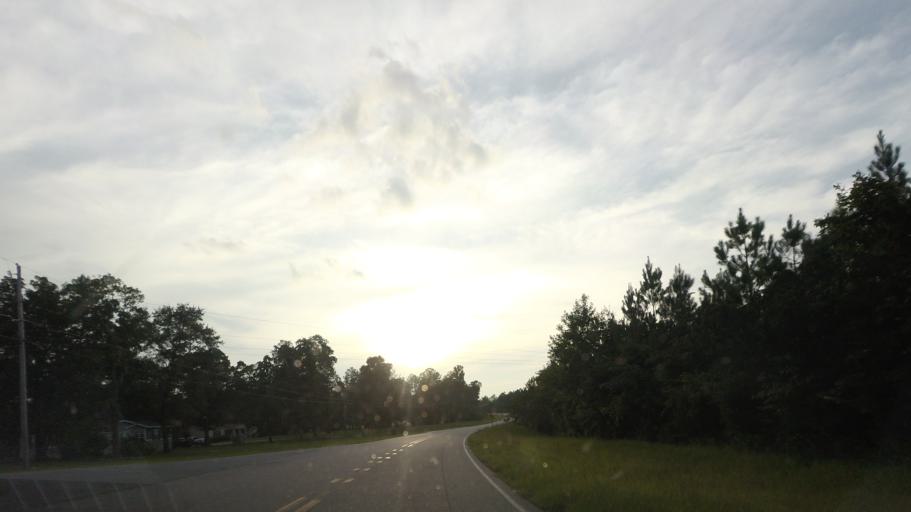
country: US
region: Georgia
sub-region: Bibb County
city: Macon
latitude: 32.8768
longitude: -83.5229
